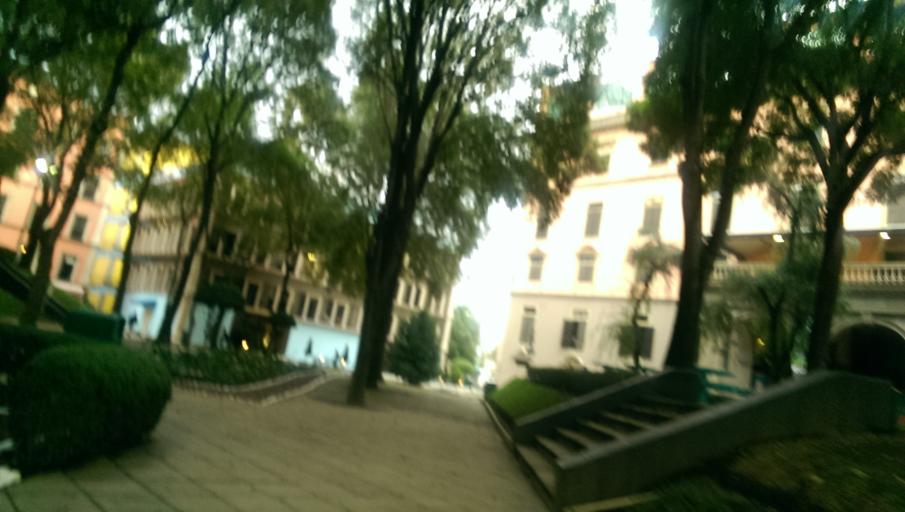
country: MX
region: Mexico City
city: Tlalpan
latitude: 19.2843
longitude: -99.1358
